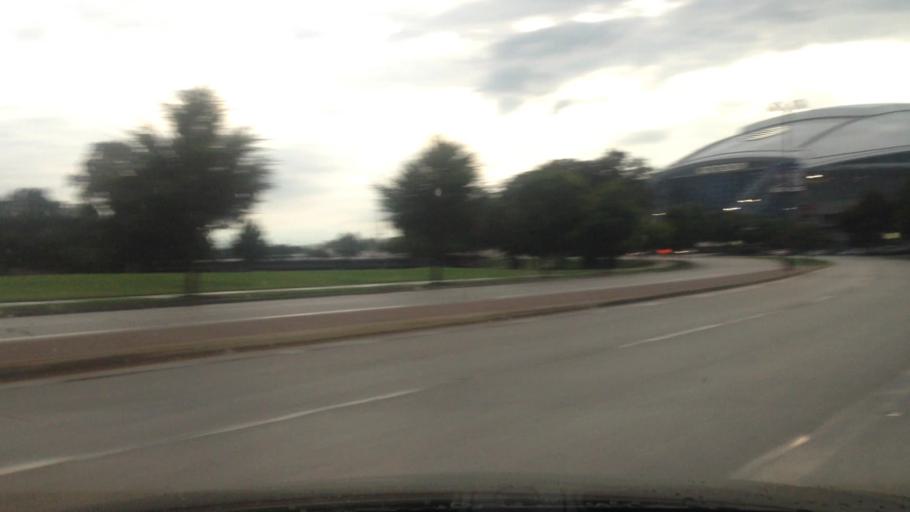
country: US
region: Texas
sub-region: Tarrant County
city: Arlington
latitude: 32.7528
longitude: -97.0883
